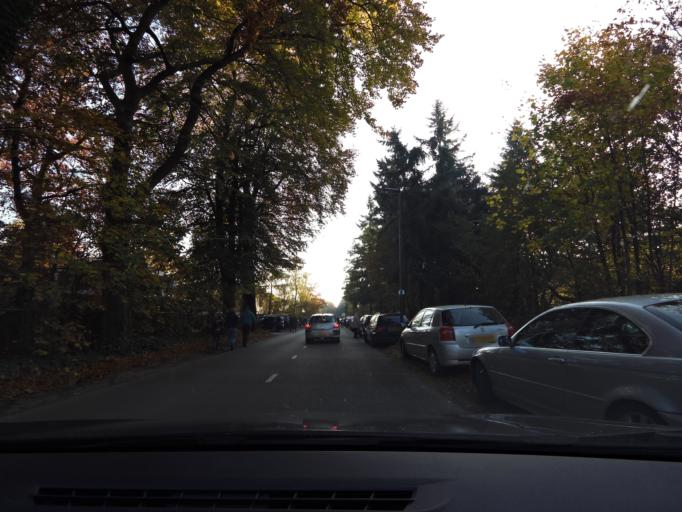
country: NL
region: North Brabant
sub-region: Gemeente Breda
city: Breda
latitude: 51.5536
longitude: 4.7801
